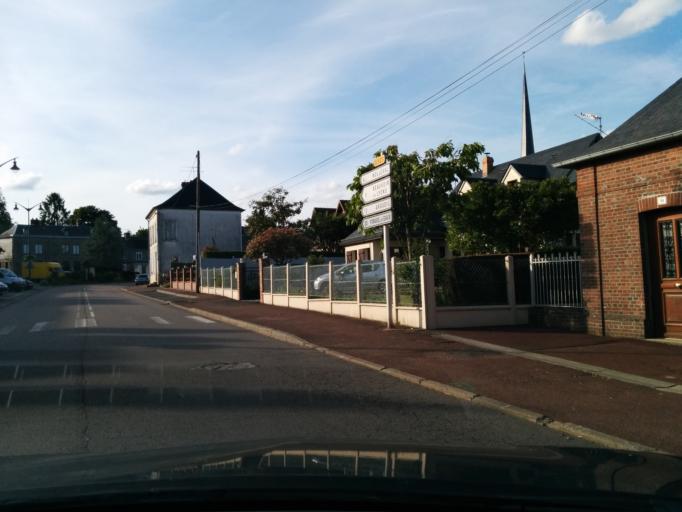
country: FR
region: Haute-Normandie
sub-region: Departement de la Seine-Maritime
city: La Feuillie
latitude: 49.4627
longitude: 1.5147
